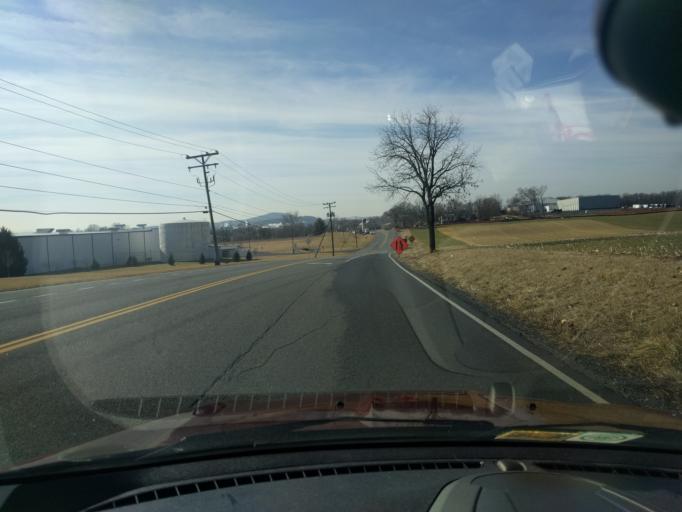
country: US
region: Virginia
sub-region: Rockingham County
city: Dayton
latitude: 38.3820
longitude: -78.9251
